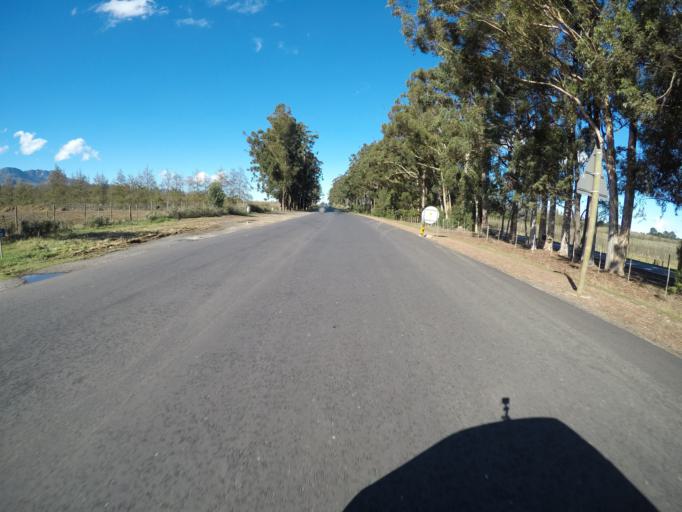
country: ZA
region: Western Cape
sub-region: Overberg District Municipality
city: Grabouw
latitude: -34.1669
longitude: 19.0398
